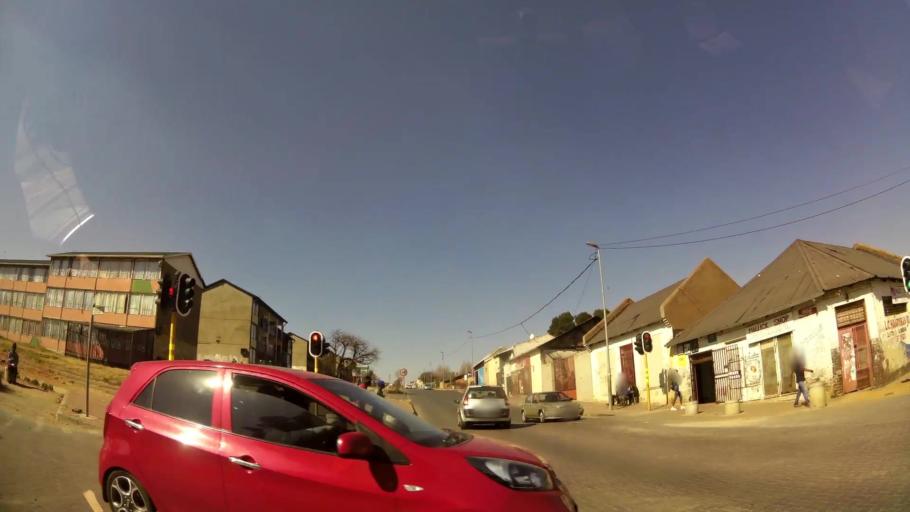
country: ZA
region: Gauteng
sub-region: City of Johannesburg Metropolitan Municipality
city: Johannesburg
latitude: -26.1834
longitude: 27.9687
